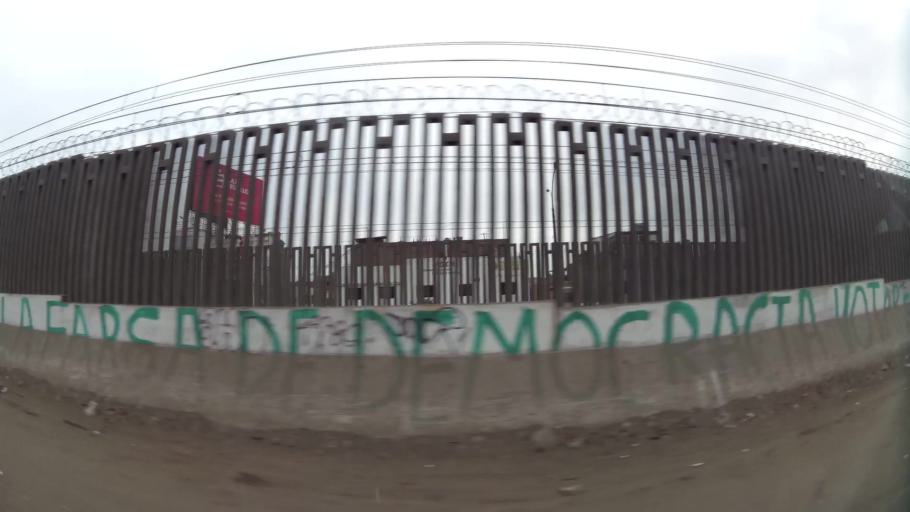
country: PE
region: Lima
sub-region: Lima
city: Surco
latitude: -12.1572
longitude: -76.9635
